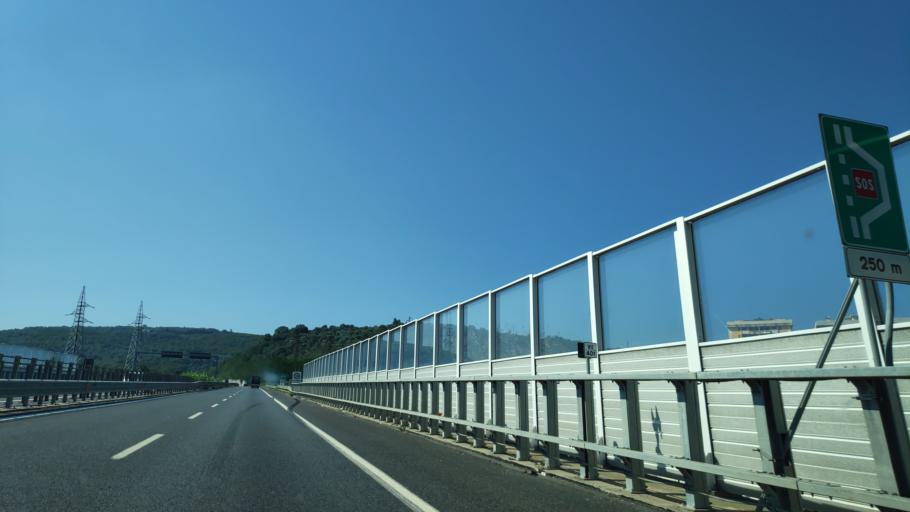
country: IT
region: Calabria
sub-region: Provincia di Reggio Calabria
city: Seminara
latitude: 38.3646
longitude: 15.8651
